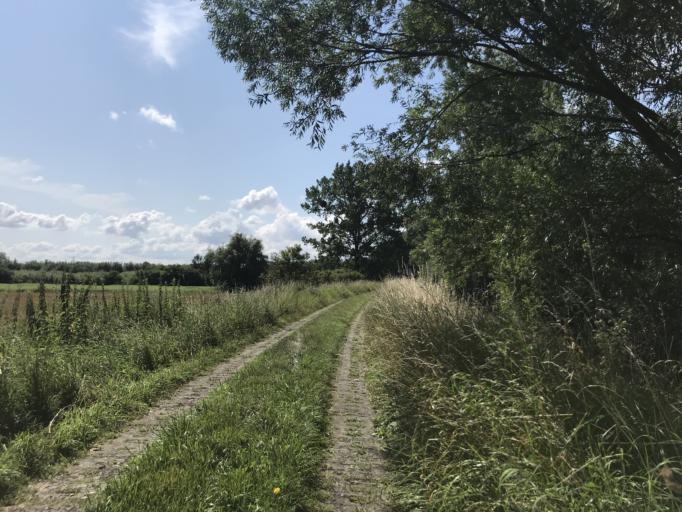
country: PL
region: Pomeranian Voivodeship
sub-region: Gdansk
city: Gdansk
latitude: 54.3230
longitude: 18.6716
